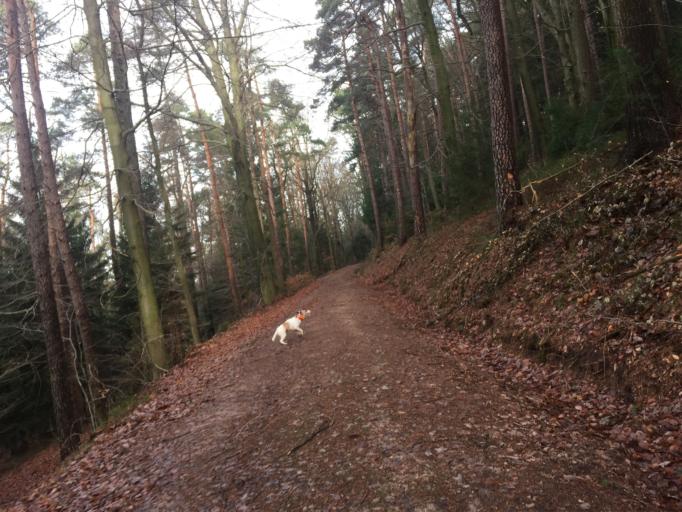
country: DE
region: Hesse
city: Reichelsheim
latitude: 49.7006
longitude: 8.8921
